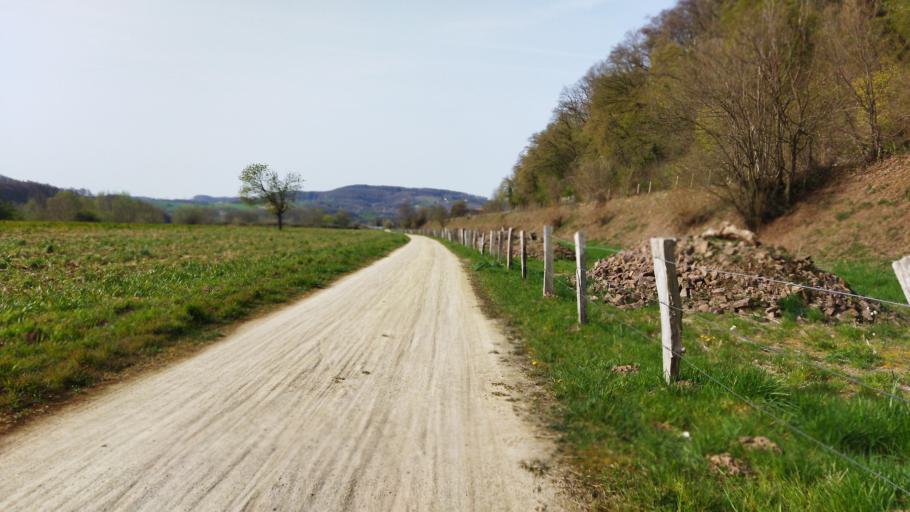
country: DE
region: North Rhine-Westphalia
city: Porta Westfalica
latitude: 52.1825
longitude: 8.9215
